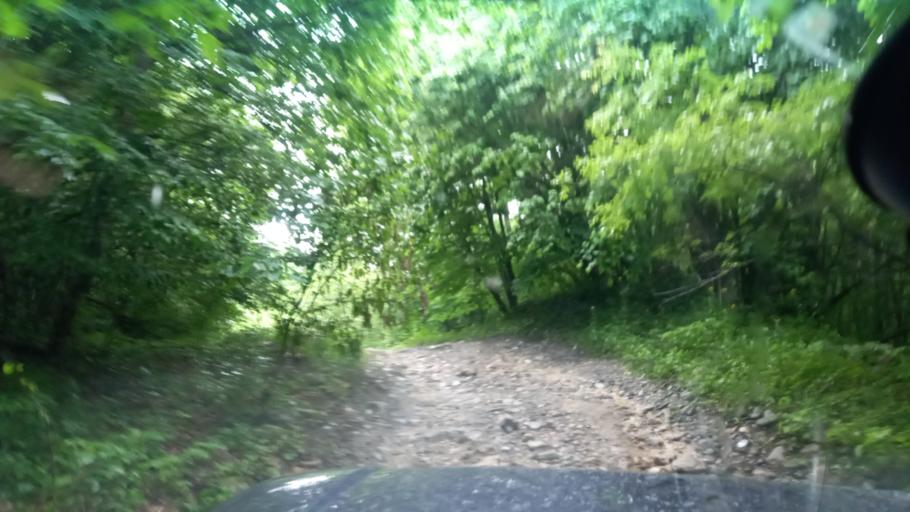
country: RU
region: Krasnodarskiy
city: Psebay
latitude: 44.0170
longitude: 40.7104
